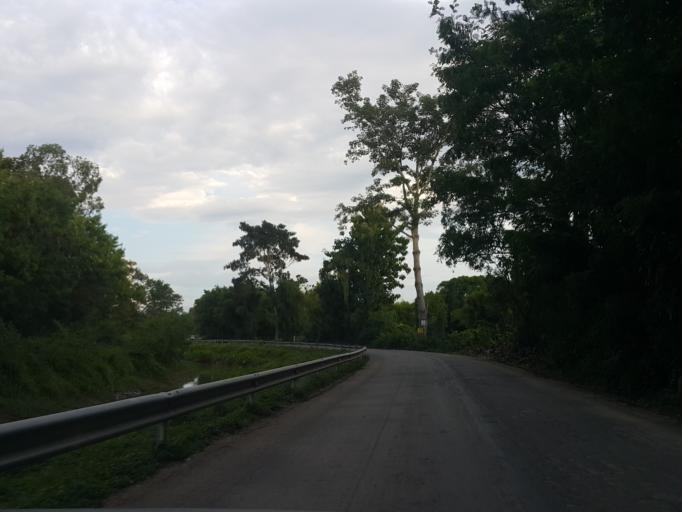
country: TH
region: Chiang Mai
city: San Sai
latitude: 18.9008
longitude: 99.0437
